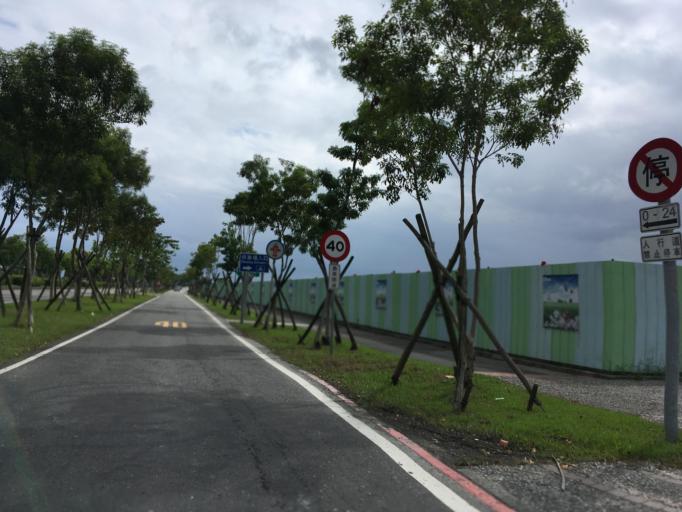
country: TW
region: Taiwan
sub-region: Yilan
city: Yilan
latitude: 24.6777
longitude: 121.7780
